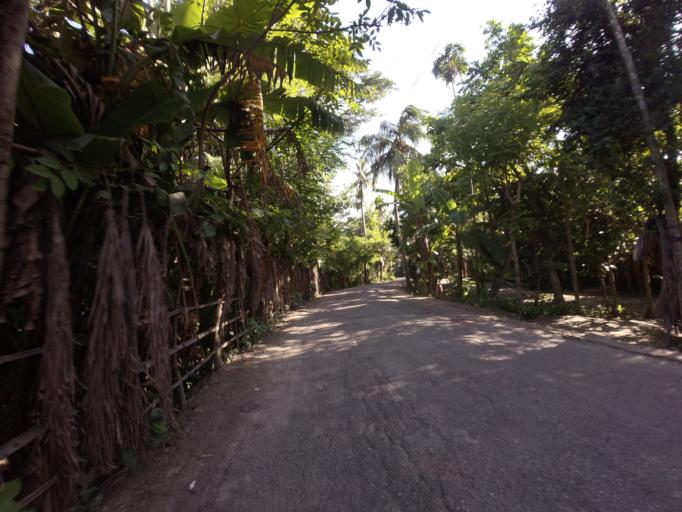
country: BD
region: Khulna
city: Kalia
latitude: 23.0029
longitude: 89.5790
